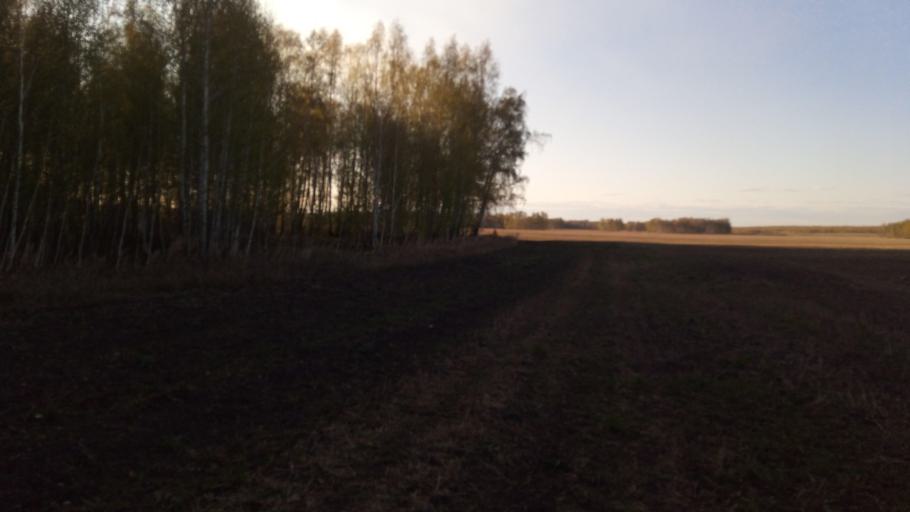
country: RU
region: Chelyabinsk
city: Timiryazevskiy
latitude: 54.9940
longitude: 60.8685
